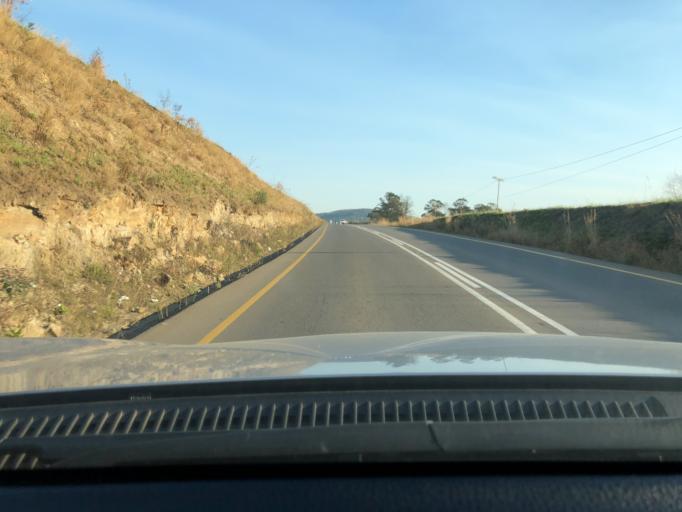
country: ZA
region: KwaZulu-Natal
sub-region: Sisonke District Municipality
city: Ixopo
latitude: -30.1724
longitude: 30.0614
